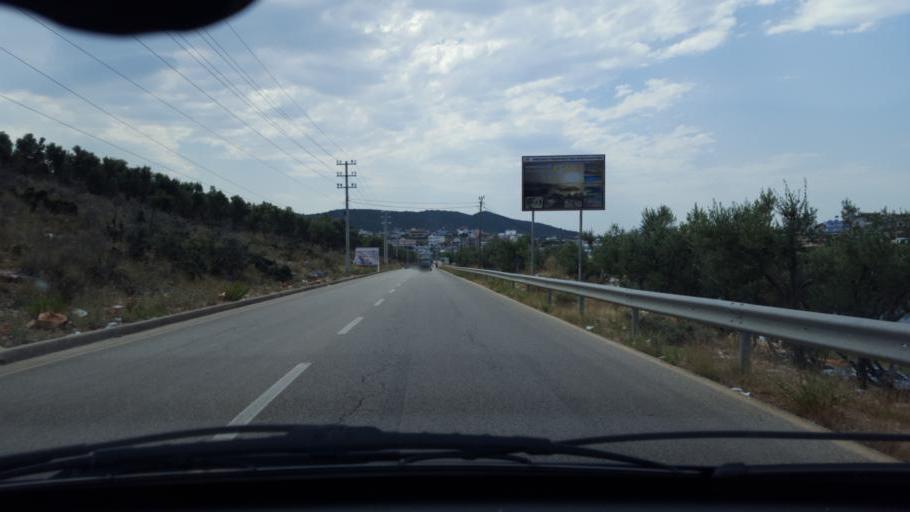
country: AL
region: Vlore
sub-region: Rrethi i Sarandes
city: Xarre
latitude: 39.7822
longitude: 20.0074
